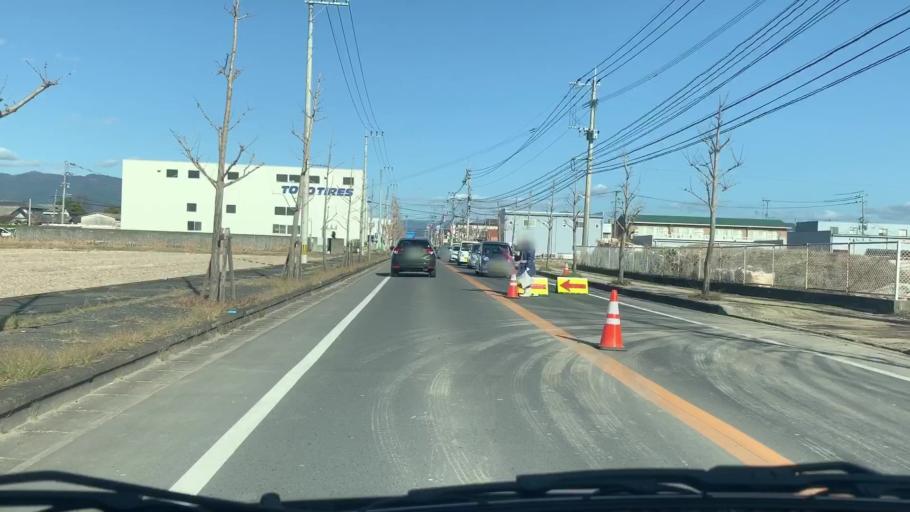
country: JP
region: Saga Prefecture
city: Saga-shi
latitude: 33.2519
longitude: 130.2647
